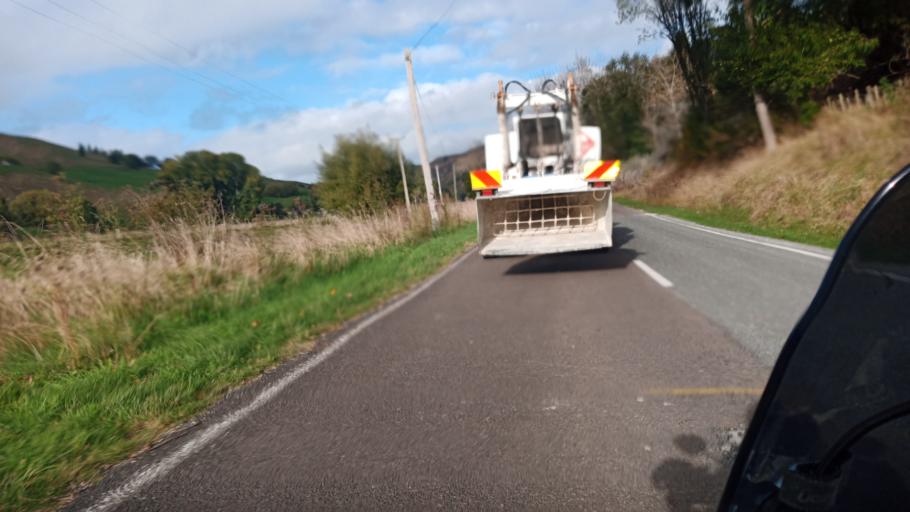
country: NZ
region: Gisborne
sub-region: Gisborne District
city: Gisborne
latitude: -38.5874
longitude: 177.7851
